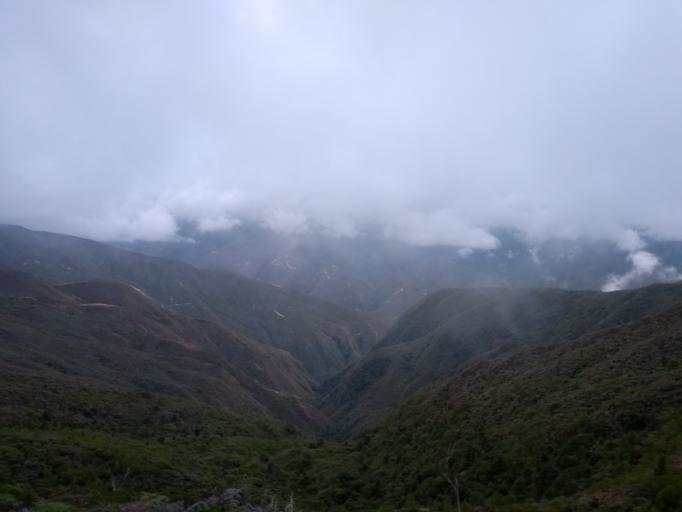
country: CO
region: Cesar
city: Manaure Balcon del Cesar
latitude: 10.1943
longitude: -73.0047
